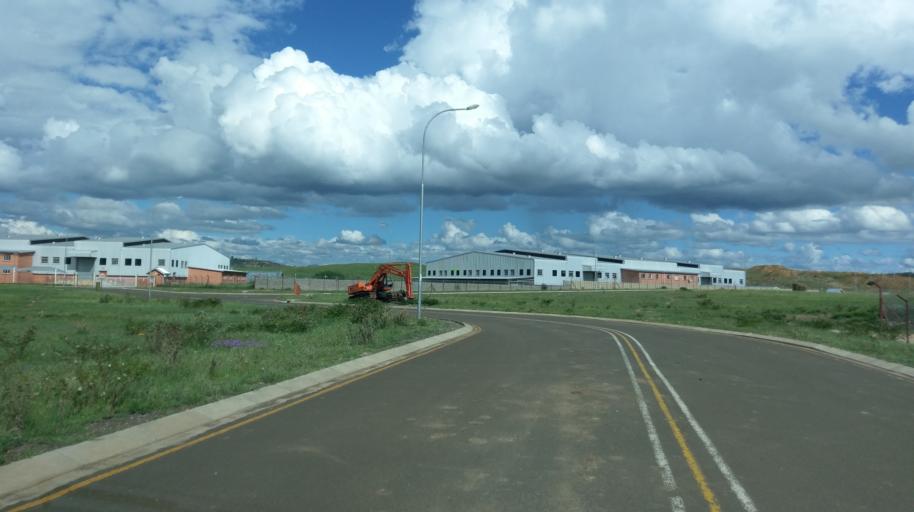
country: LS
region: Maseru
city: Maseru
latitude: -29.3828
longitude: 27.4851
